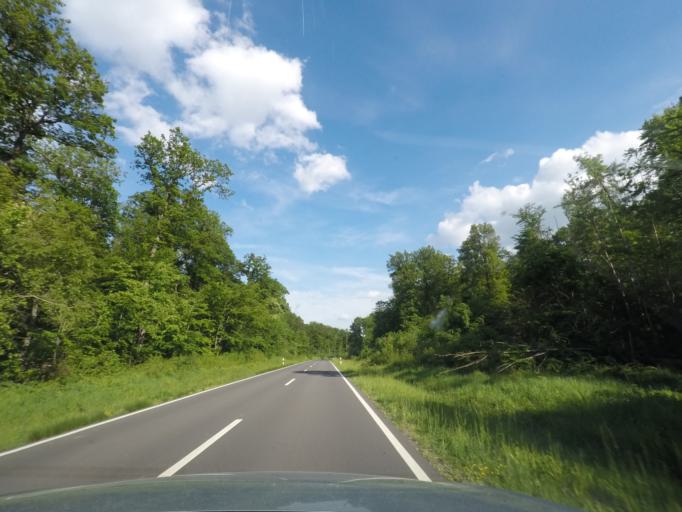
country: DE
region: Lower Saxony
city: Twieflingen
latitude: 52.1515
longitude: 10.9319
